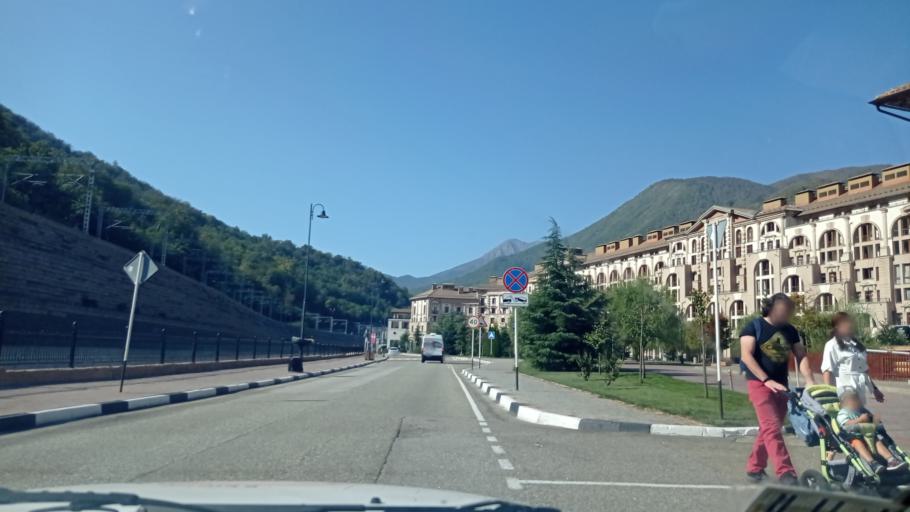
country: RU
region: Krasnodarskiy
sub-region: Sochi City
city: Krasnaya Polyana
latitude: 43.6823
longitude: 40.2612
